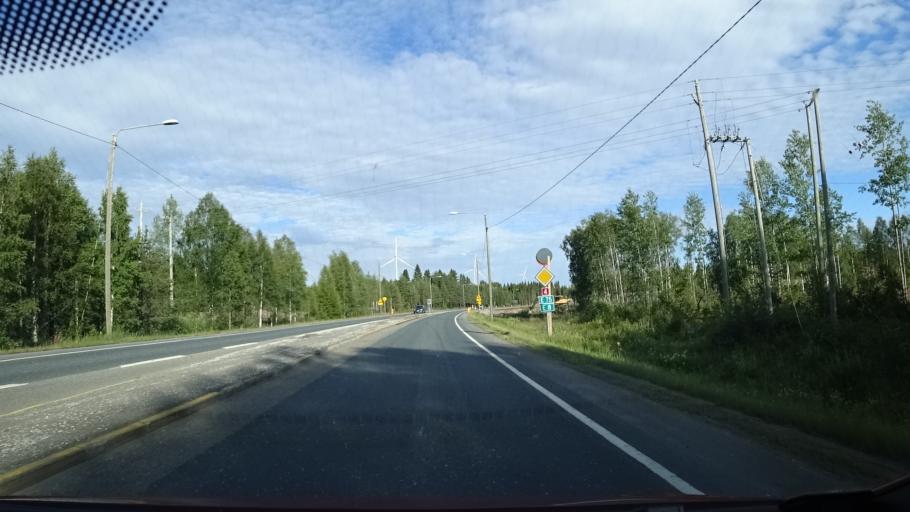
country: FI
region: Lapland
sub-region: Kemi-Tornio
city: Simo
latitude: 65.6575
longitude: 25.0785
